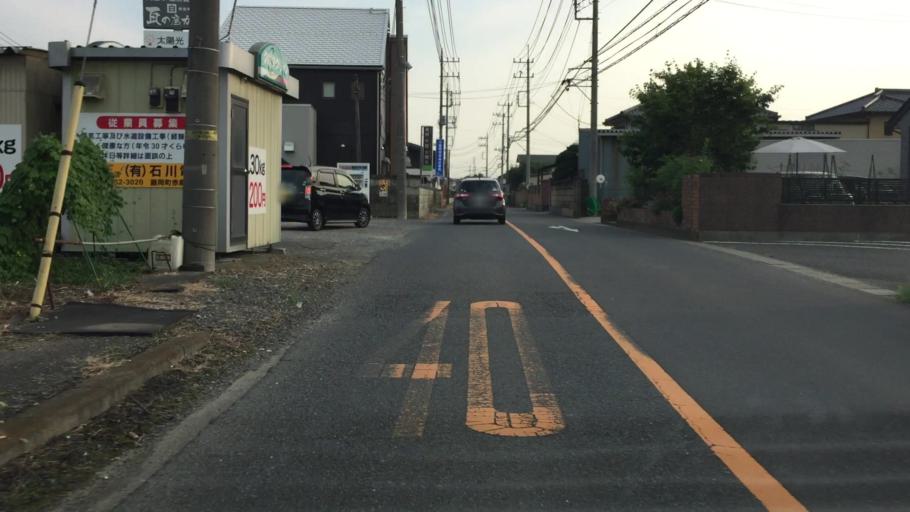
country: JP
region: Tochigi
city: Fujioka
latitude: 36.2755
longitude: 139.6563
